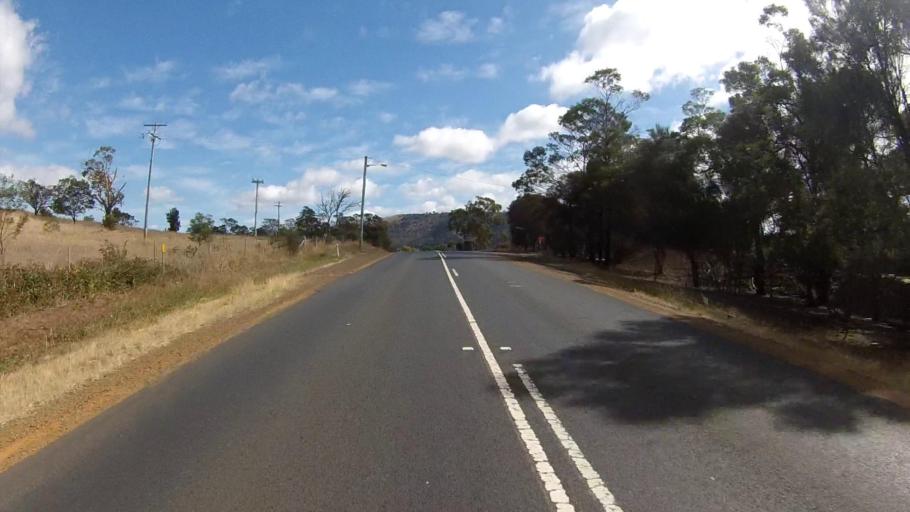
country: AU
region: Tasmania
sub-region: Brighton
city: Old Beach
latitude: -42.7304
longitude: 147.2886
